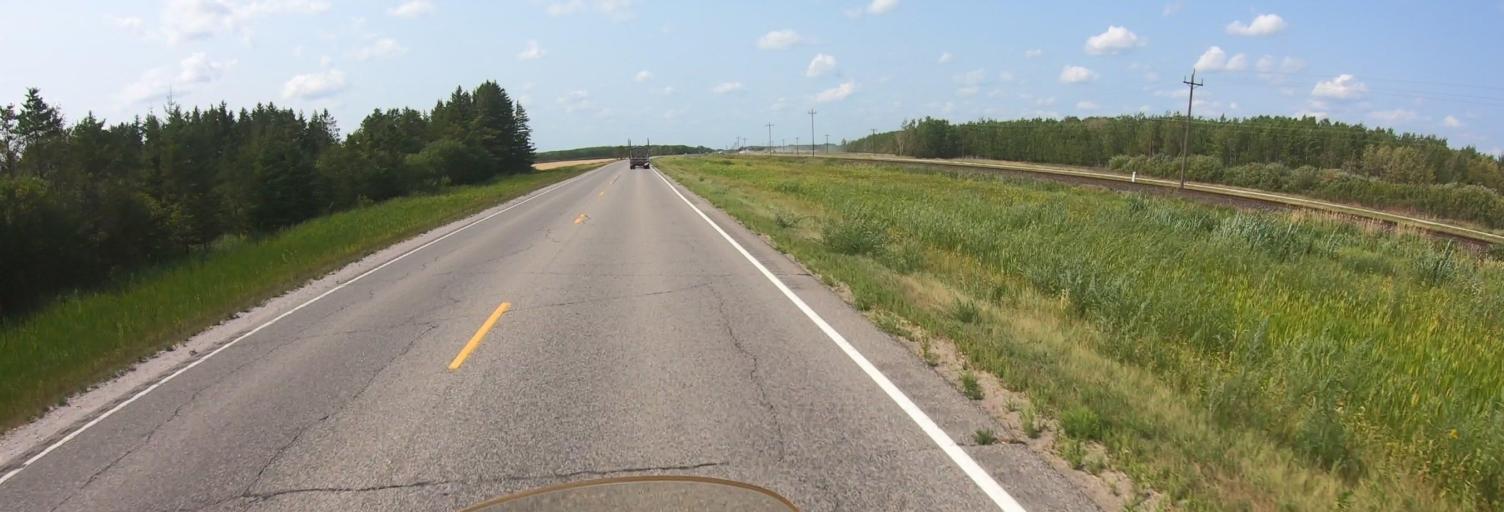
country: US
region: Minnesota
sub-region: Roseau County
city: Warroad
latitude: 48.8743
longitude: -95.2735
